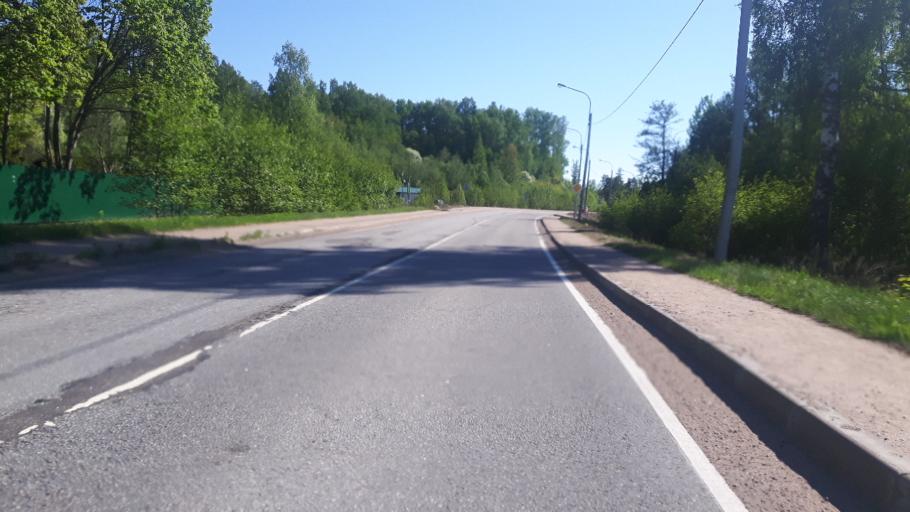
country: RU
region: Leningrad
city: Sosnovyy Bor
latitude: 60.2143
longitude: 29.0077
